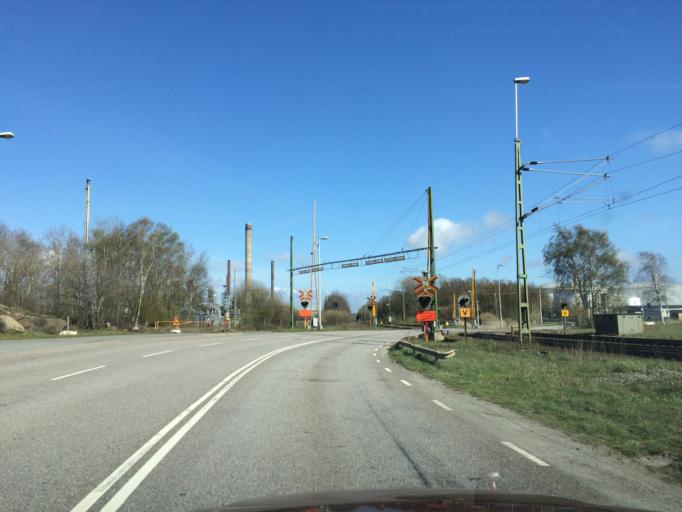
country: SE
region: Vaestra Goetaland
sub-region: Goteborg
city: Majorna
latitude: 57.6999
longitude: 11.8680
